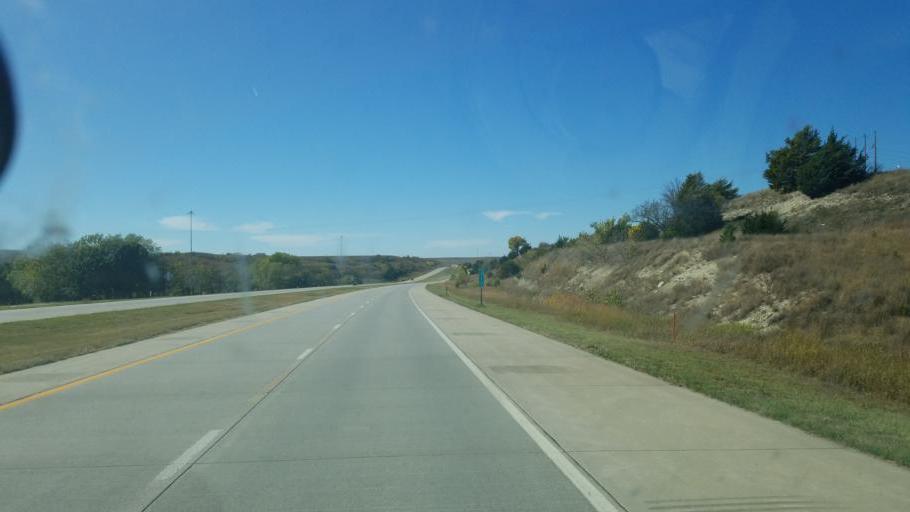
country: US
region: Kansas
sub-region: Riley County
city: Ogden
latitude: 39.0657
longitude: -96.6119
